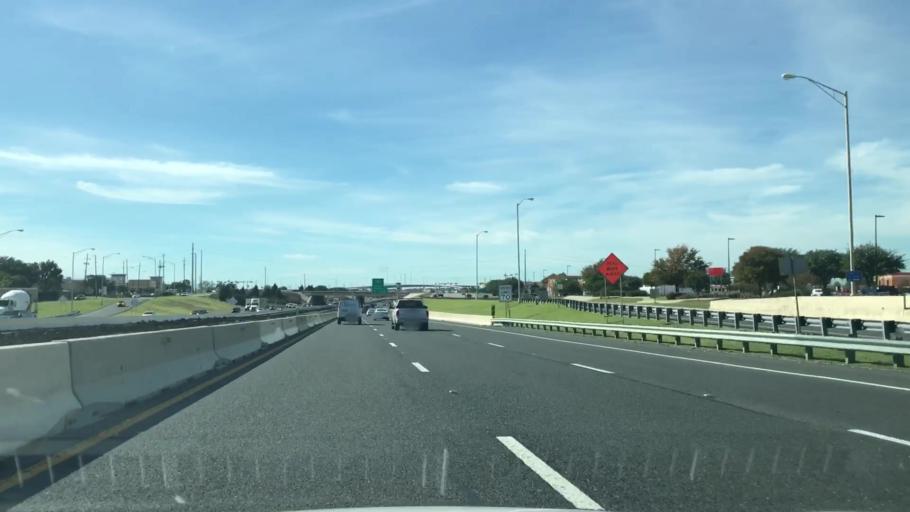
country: US
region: Texas
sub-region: Dallas County
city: Carrollton
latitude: 32.9838
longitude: -96.9044
